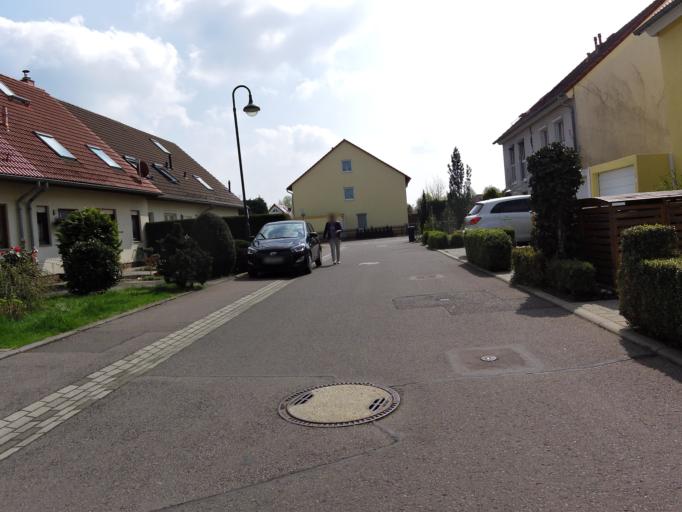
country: DE
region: Saxony
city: Markranstadt
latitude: 51.3256
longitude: 12.2583
